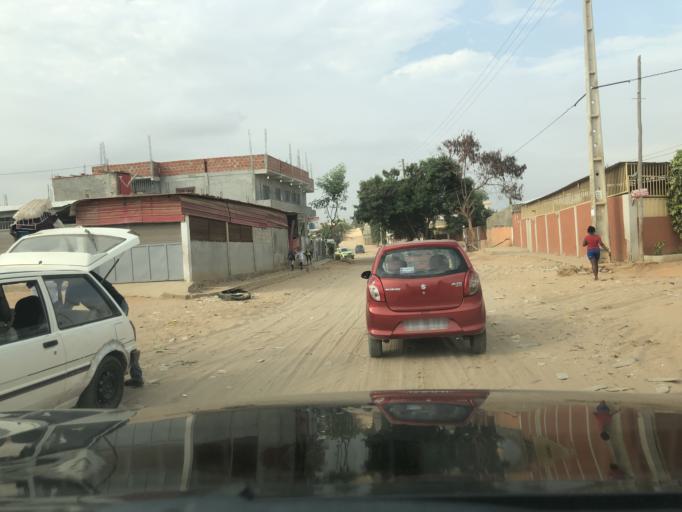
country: AO
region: Luanda
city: Luanda
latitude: -8.9274
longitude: 13.2293
